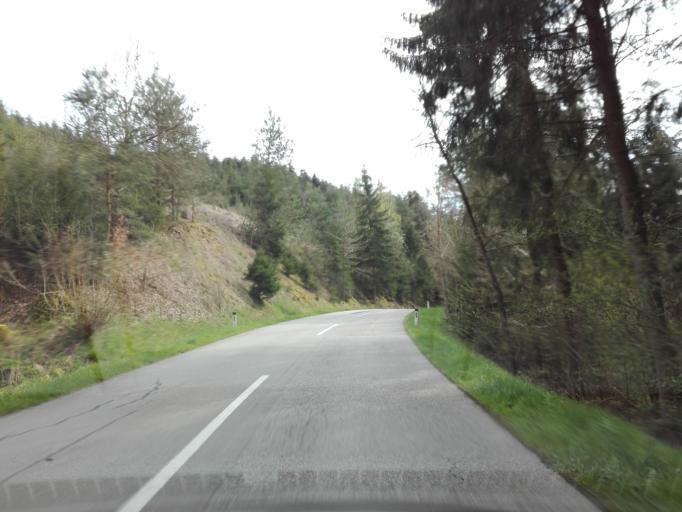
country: AT
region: Upper Austria
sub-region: Politischer Bezirk Rohrbach
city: Atzesberg
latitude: 48.5296
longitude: 13.9451
